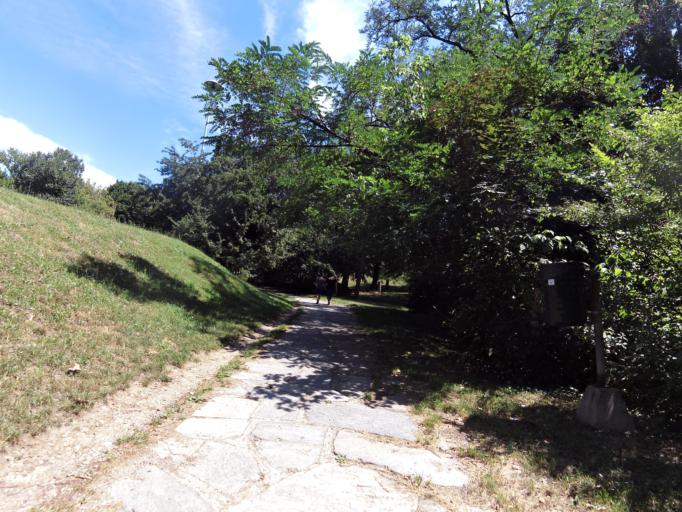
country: IT
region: Lombardy
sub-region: Citta metropolitana di Milano
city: Sesto San Giovanni
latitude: 45.4942
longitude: 9.2454
